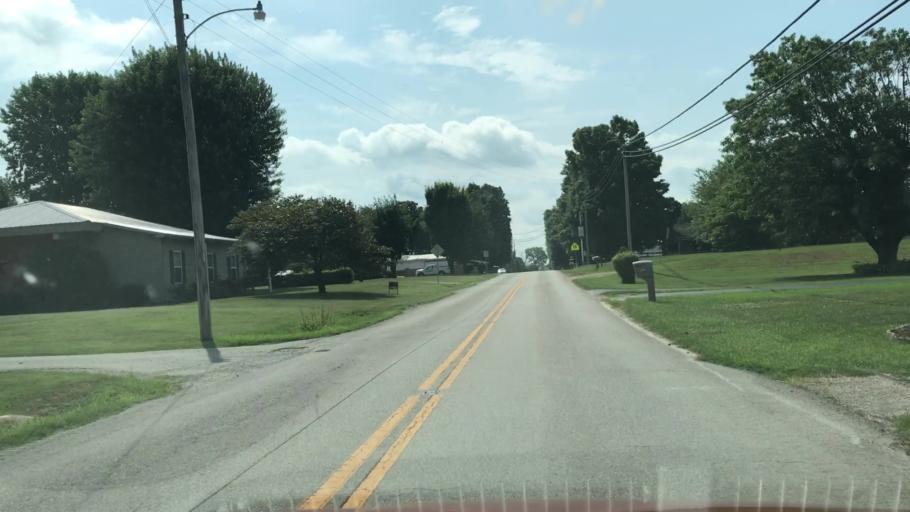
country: US
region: Kentucky
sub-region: Barren County
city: Glasgow
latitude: 36.8882
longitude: -85.8495
